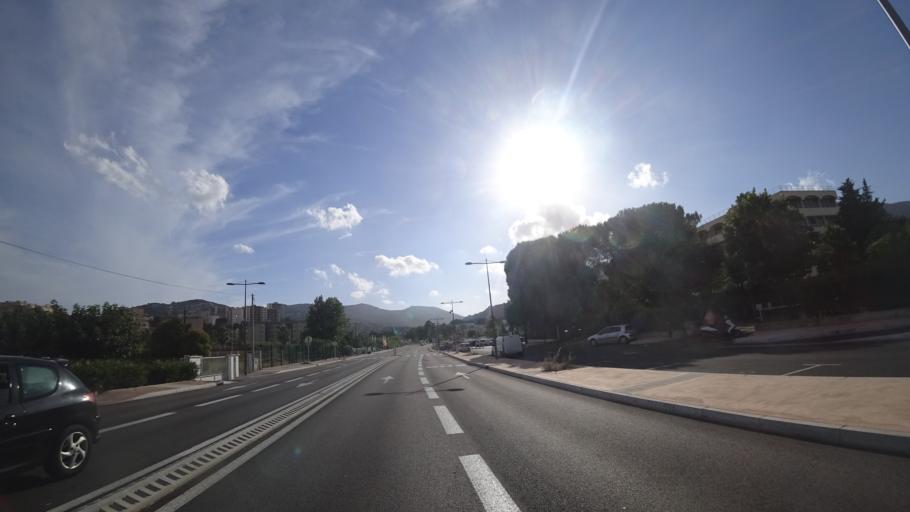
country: FR
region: Corsica
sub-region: Departement de la Corse-du-Sud
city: Ajaccio
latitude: 41.9377
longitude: 8.7388
